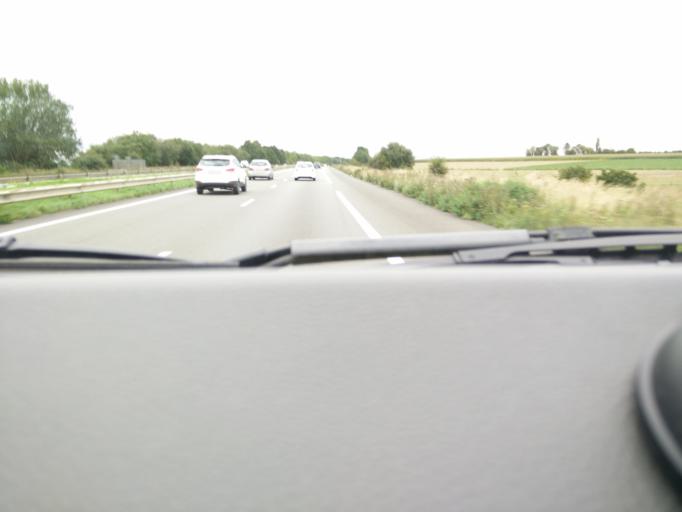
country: FR
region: Nord-Pas-de-Calais
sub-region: Departement du Nord
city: Sainghin-en-Melantois
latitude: 50.5766
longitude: 3.1527
